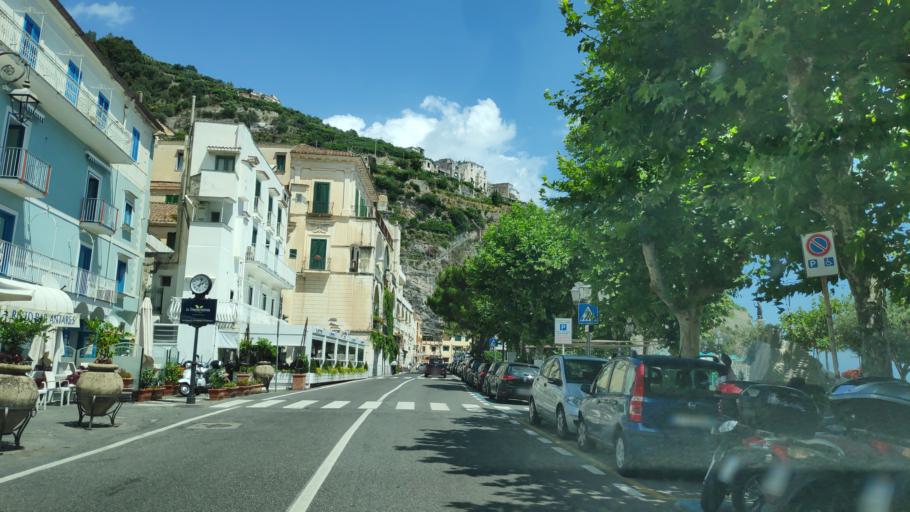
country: IT
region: Campania
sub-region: Provincia di Salerno
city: Minori
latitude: 40.6494
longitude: 14.6266
